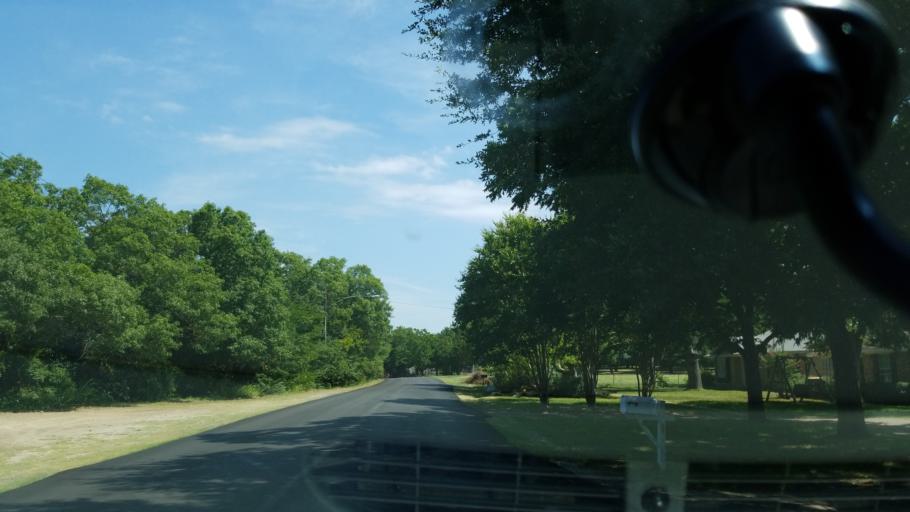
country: US
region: Texas
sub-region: Dallas County
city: Cockrell Hill
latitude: 32.7094
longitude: -96.8814
